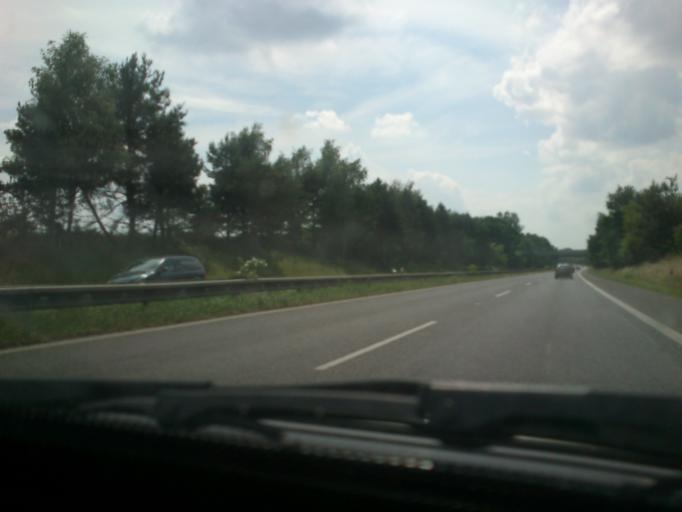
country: CZ
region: Central Bohemia
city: Benatky nad Jizerou
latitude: 50.2753
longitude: 14.8206
